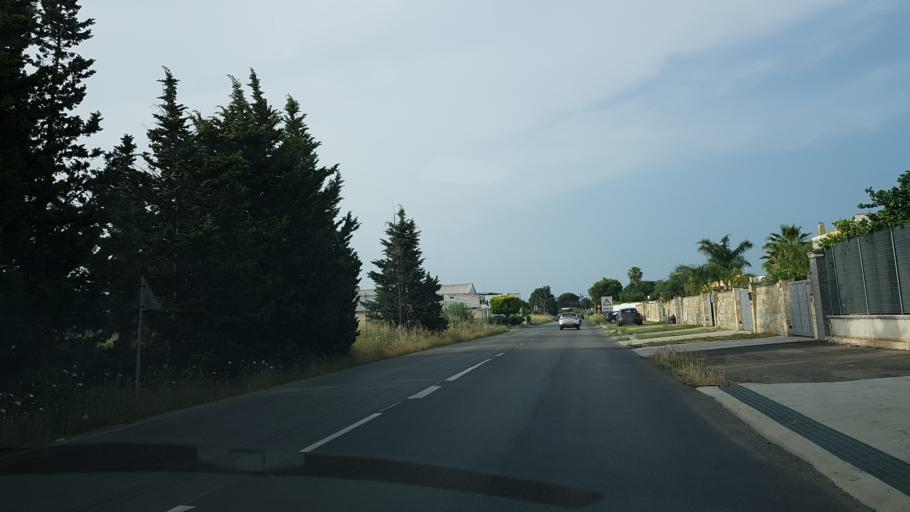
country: IT
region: Apulia
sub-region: Provincia di Brindisi
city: San Pietro Vernotico
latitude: 40.4956
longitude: 17.9915
